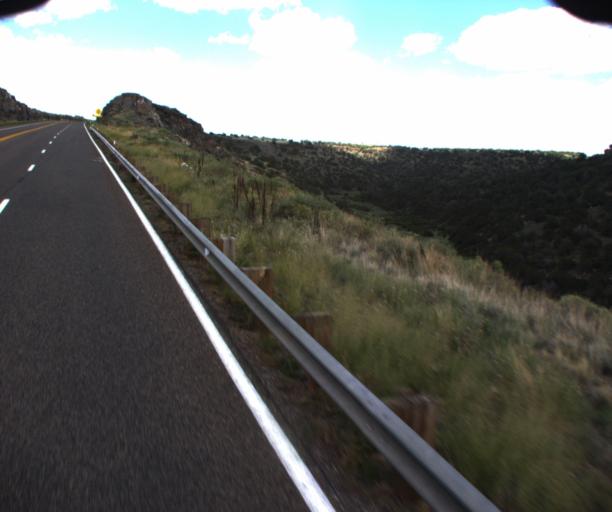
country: US
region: Arizona
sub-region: Apache County
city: Springerville
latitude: 34.1417
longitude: -109.2268
